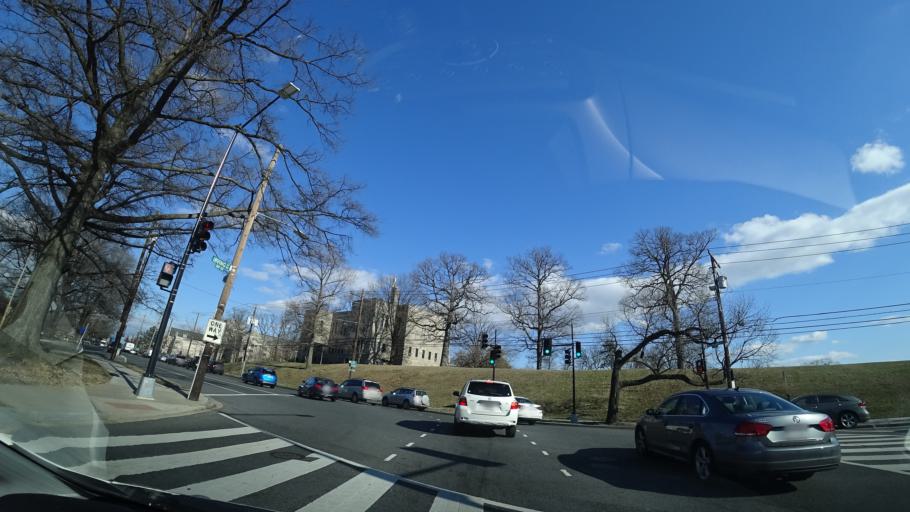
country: US
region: Maryland
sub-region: Prince George's County
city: Chillum
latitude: 38.9304
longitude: -77.0029
